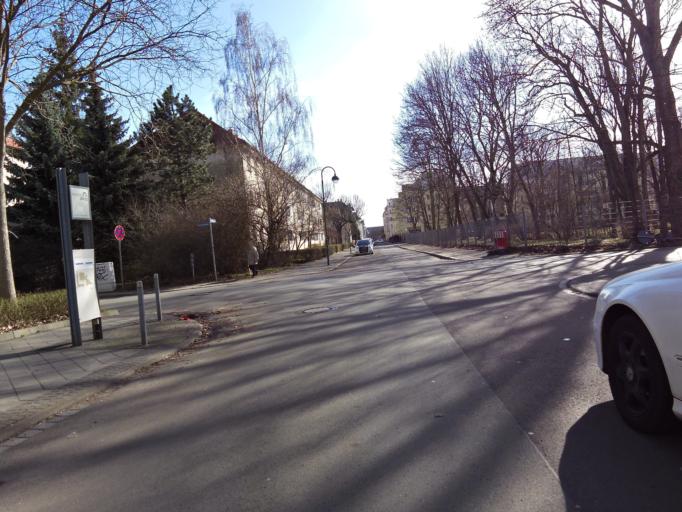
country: DE
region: Saxony
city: Leipzig
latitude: 51.3494
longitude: 12.3522
